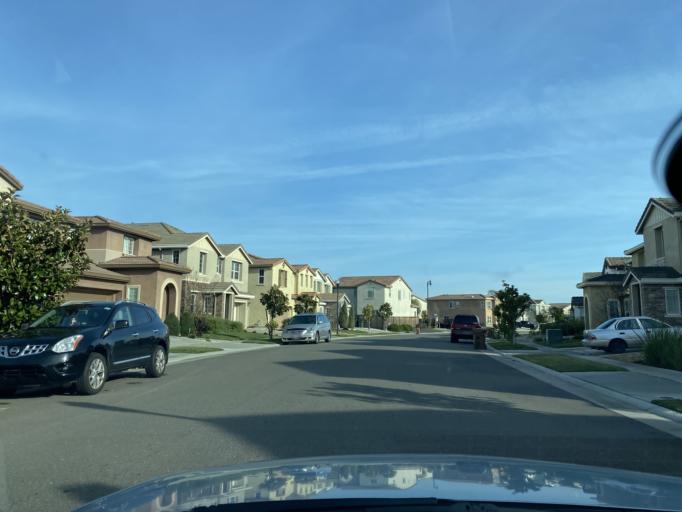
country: US
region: California
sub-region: Sacramento County
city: Elk Grove
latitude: 38.3986
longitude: -121.3920
